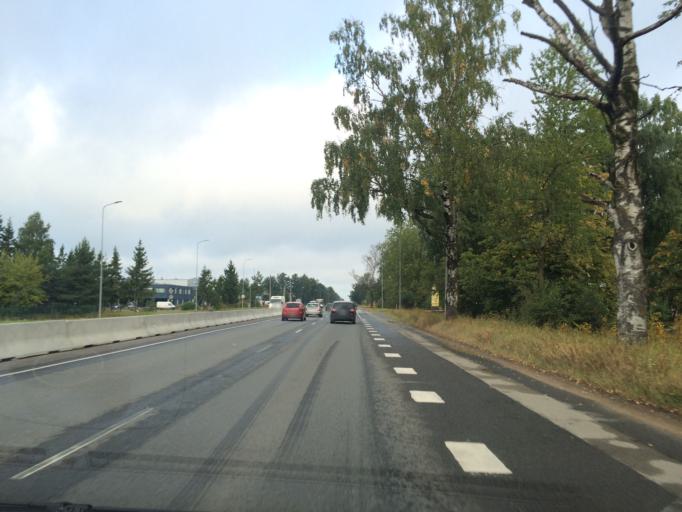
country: LV
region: Kekava
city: Kekava
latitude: 56.8768
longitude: 24.2589
